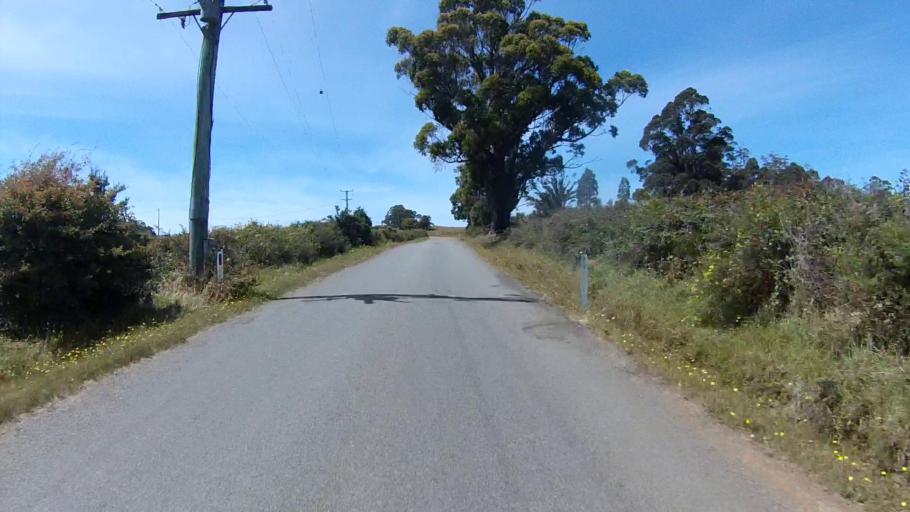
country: AU
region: Tasmania
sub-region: Sorell
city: Sorell
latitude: -42.7059
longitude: 147.7448
